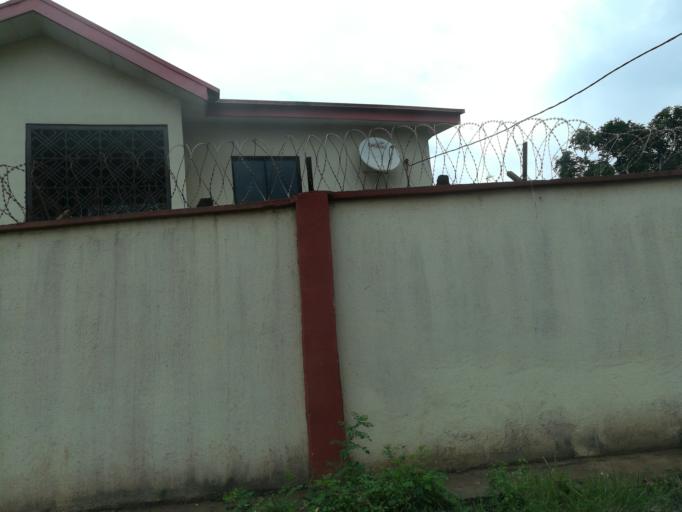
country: NG
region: Lagos
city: Agege
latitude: 6.6054
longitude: 3.3075
